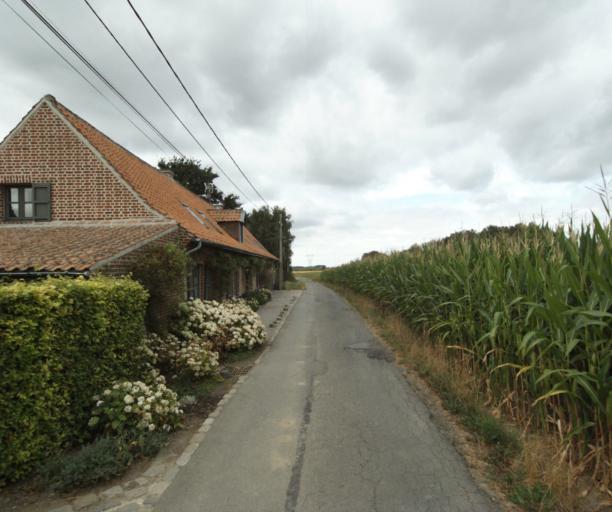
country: FR
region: Nord-Pas-de-Calais
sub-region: Departement du Nord
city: Linselles
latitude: 50.7290
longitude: 3.0978
